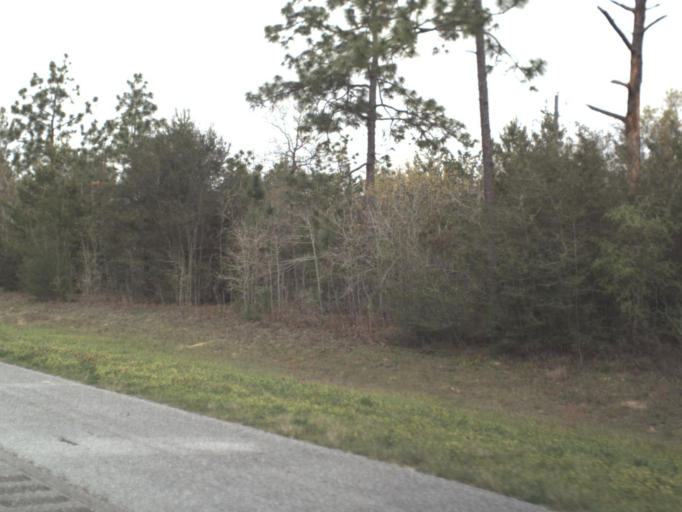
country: US
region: Florida
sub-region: Okaloosa County
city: Crestview
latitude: 30.7266
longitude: -86.4929
